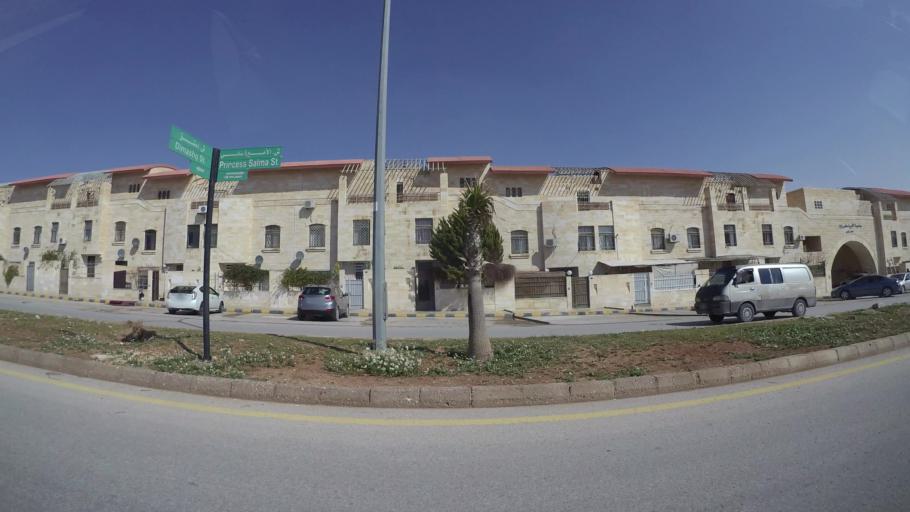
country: JO
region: Zarqa
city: Zarqa
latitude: 32.0718
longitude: 36.1073
